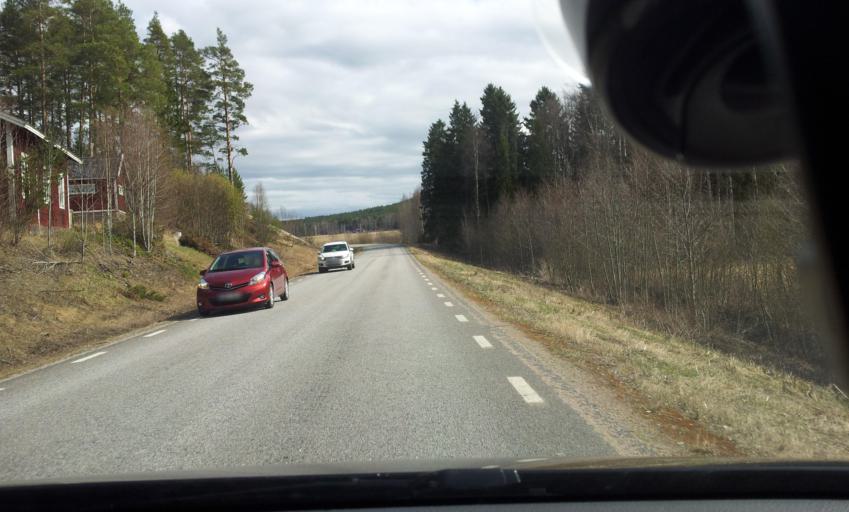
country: SE
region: Gaevleborg
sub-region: Ljusdals Kommun
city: Ljusdal
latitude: 61.7688
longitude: 15.9749
